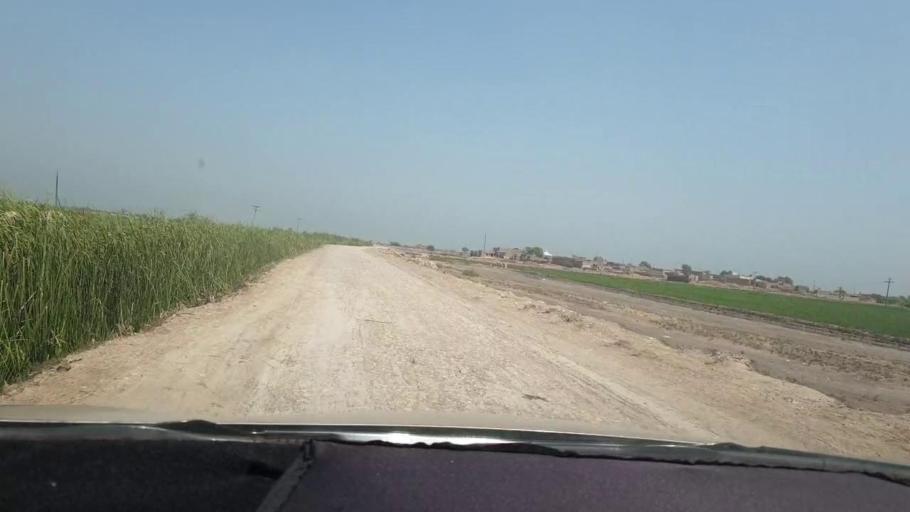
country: PK
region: Sindh
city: Shahdadkot
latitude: 27.8379
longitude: 67.9990
